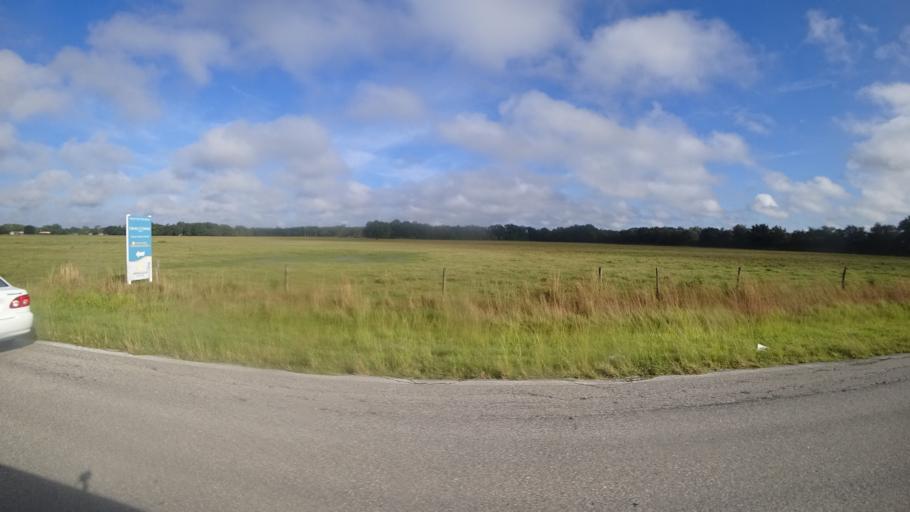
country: US
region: Florida
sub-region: Manatee County
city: Ellenton
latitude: 27.5574
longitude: -82.4184
